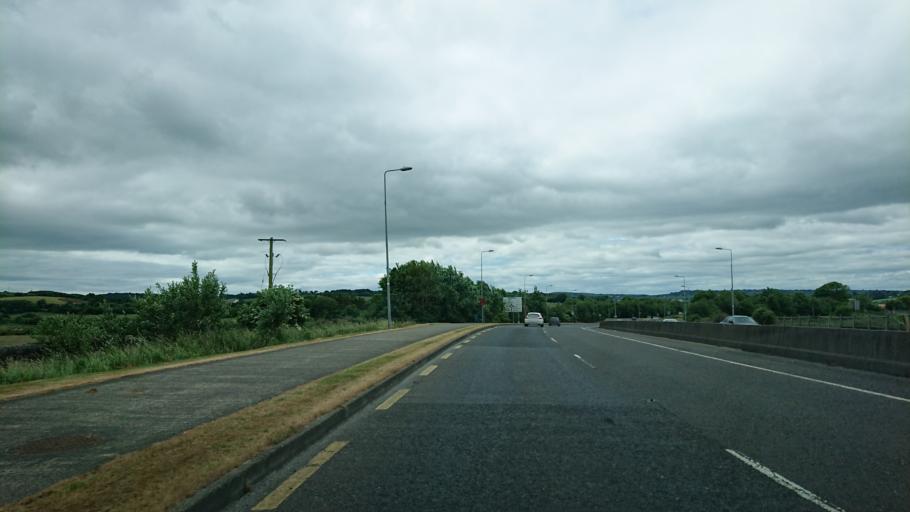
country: IE
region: Munster
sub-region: Waterford
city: Waterford
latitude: 52.2352
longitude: -7.1006
